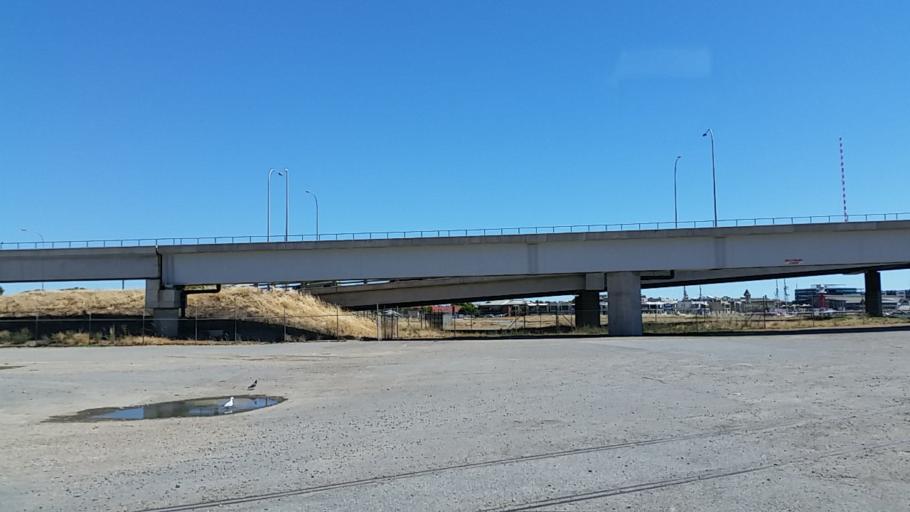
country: AU
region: South Australia
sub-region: Port Adelaide Enfield
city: Birkenhead
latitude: -34.8380
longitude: 138.5085
